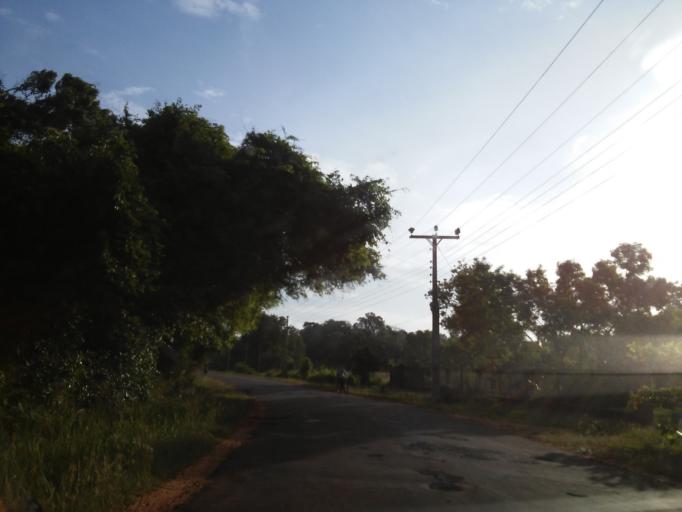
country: LK
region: Central
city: Sigiriya
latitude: 8.1512
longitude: 80.6476
